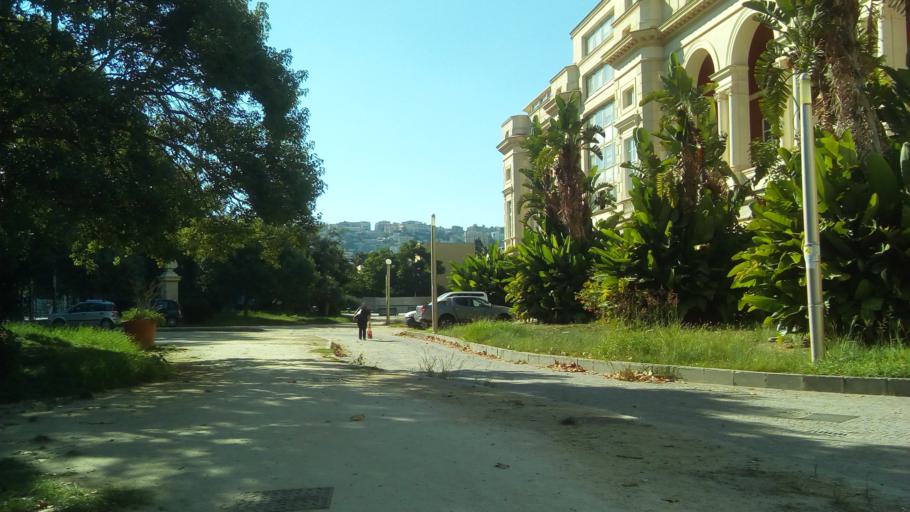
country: IT
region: Campania
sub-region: Provincia di Napoli
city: Napoli
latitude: 40.8323
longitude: 14.2398
